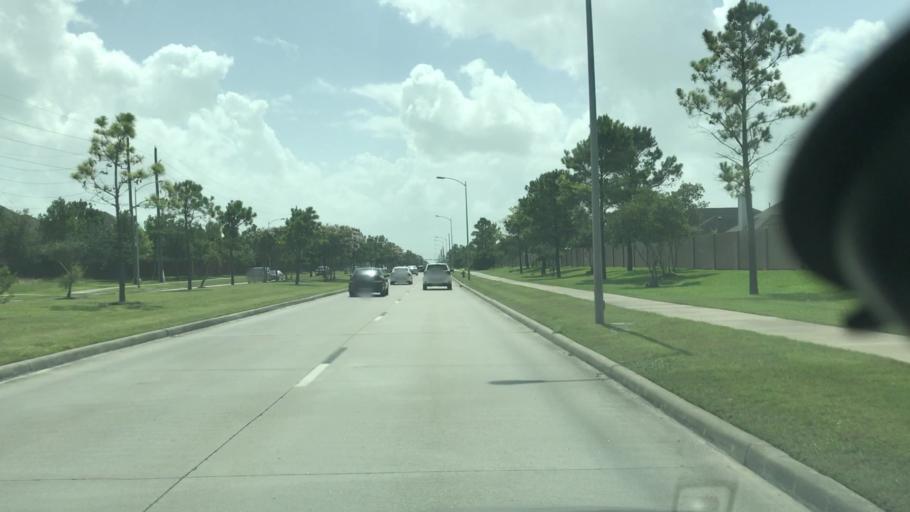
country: US
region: Texas
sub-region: Fort Bend County
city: Fresno
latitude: 29.5555
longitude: -95.4111
